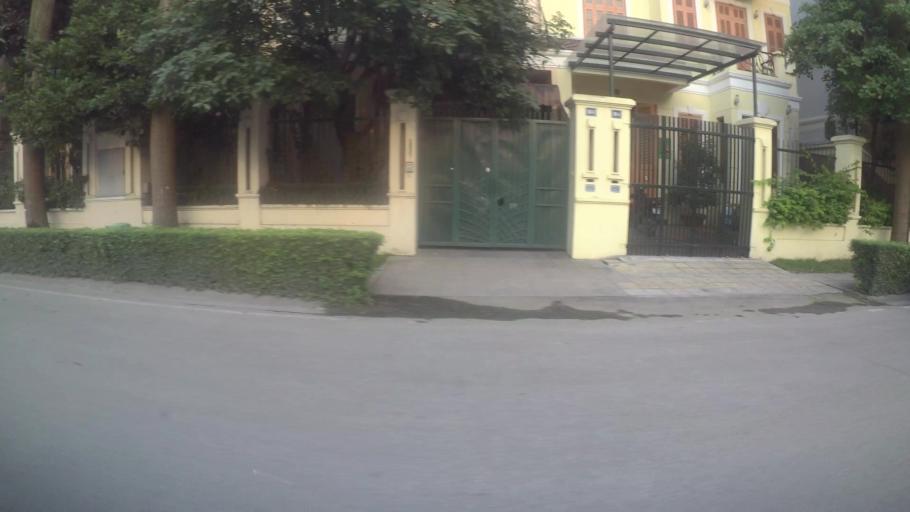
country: VN
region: Ha Noi
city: Tay Ho
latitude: 21.0730
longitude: 105.8086
